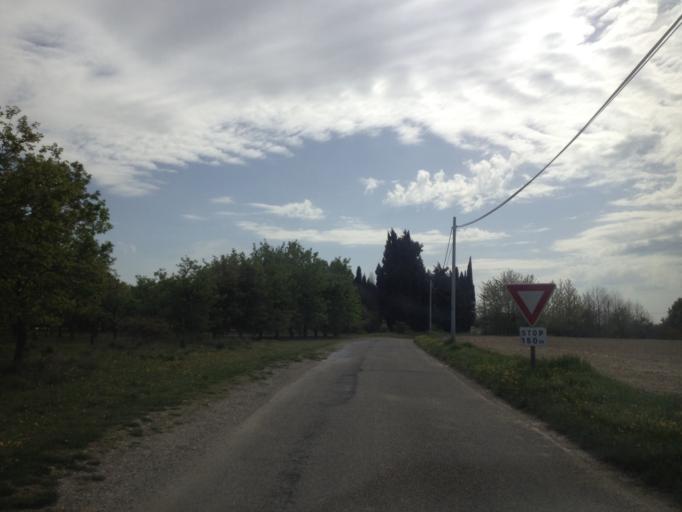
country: FR
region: Provence-Alpes-Cote d'Azur
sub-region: Departement du Vaucluse
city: Caderousse
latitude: 44.1195
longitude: 4.7818
